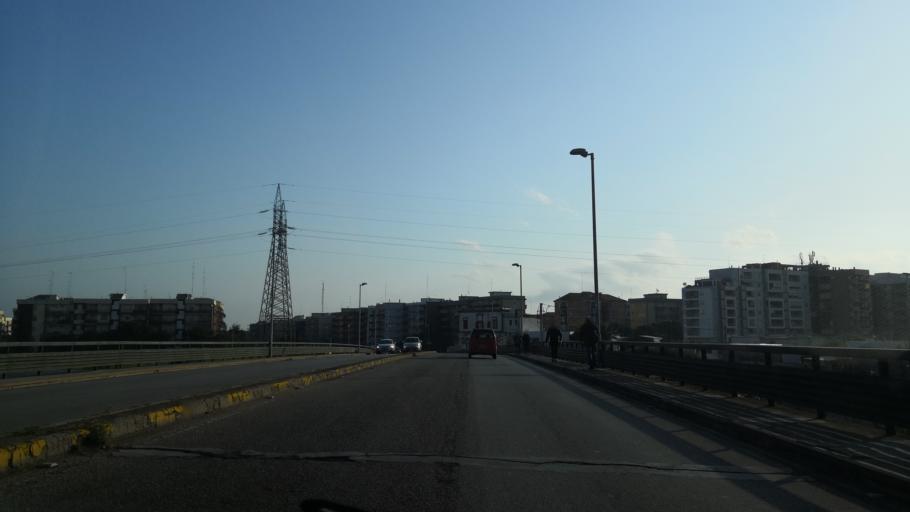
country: IT
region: Apulia
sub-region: Provincia di Bari
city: Bari
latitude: 41.1089
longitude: 16.8884
